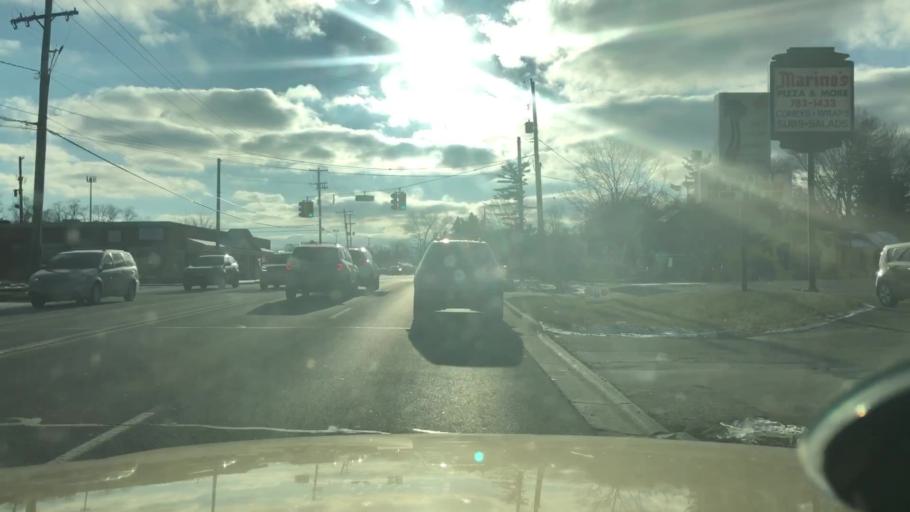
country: US
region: Michigan
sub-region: Jackson County
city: Vandercook Lake
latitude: 42.2021
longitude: -84.4367
